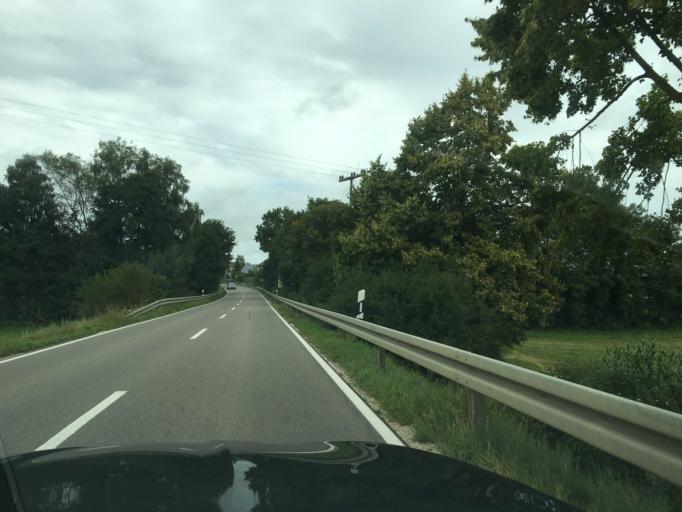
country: DE
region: Bavaria
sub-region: Swabia
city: Altenmunster
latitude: 48.4723
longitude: 10.5870
